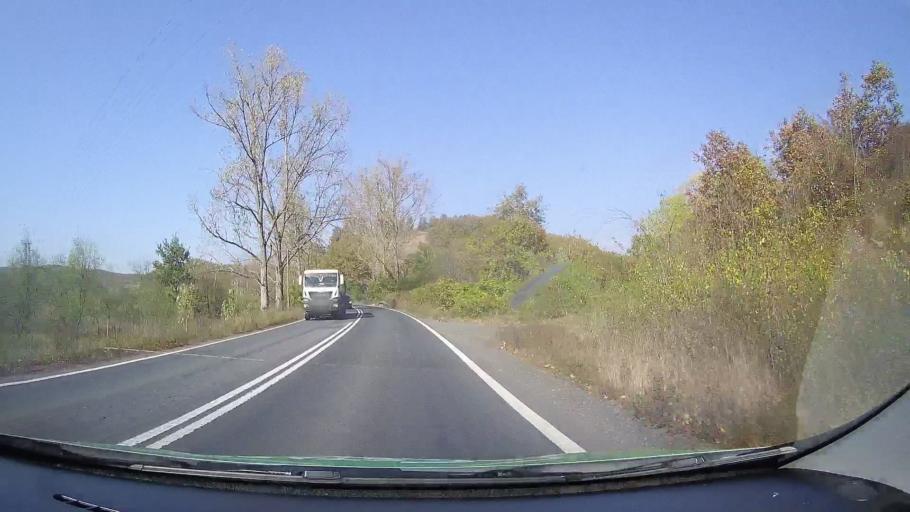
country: RO
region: Arad
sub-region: Comuna Petris
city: Petris
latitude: 46.0052
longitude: 22.3340
